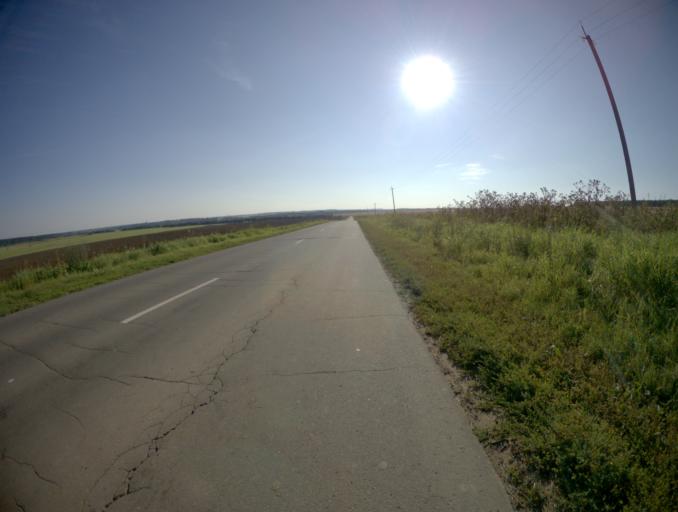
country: RU
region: Vladimir
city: Bogolyubovo
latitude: 56.2940
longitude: 40.5511
